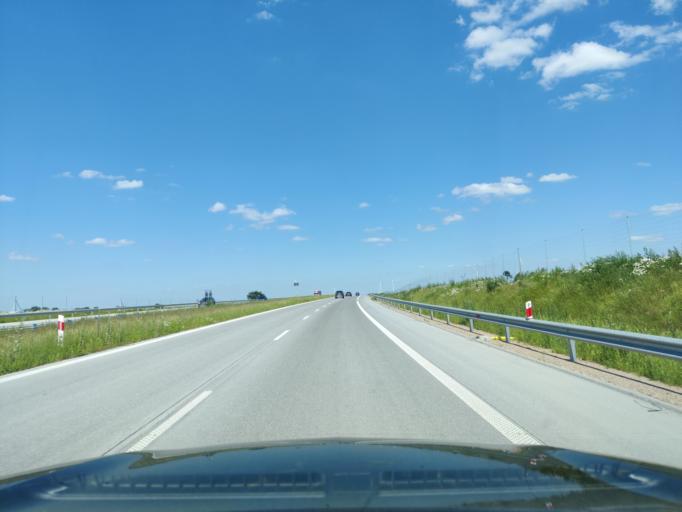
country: PL
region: Masovian Voivodeship
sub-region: Powiat mlawski
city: Wisniewo
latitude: 53.0169
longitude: 20.3387
